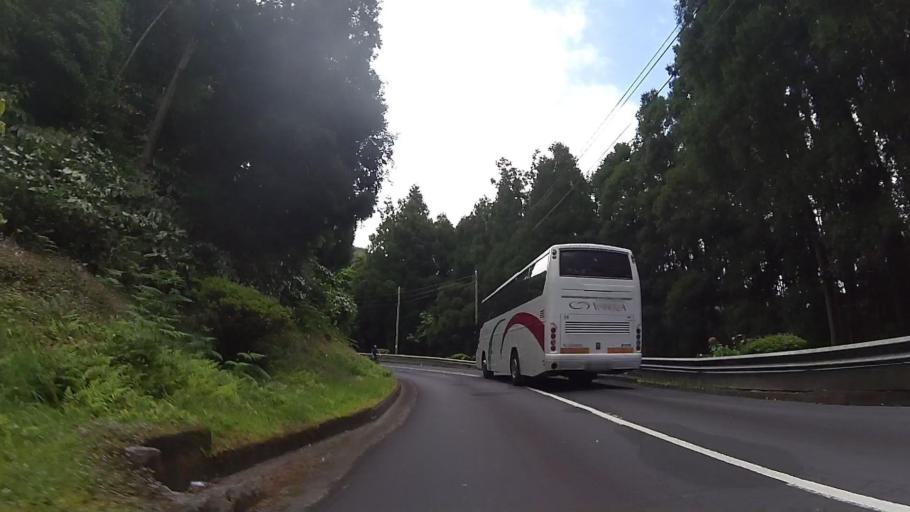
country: PT
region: Azores
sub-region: Povoacao
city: Furnas
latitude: 37.7641
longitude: -25.2883
